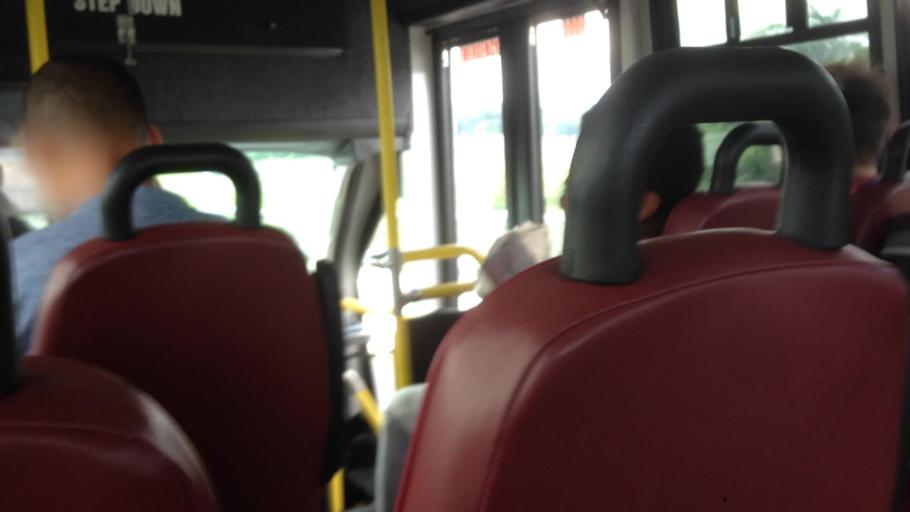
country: US
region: New York
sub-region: Ulster County
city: Lake Katrine
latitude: 41.9812
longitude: -73.9588
